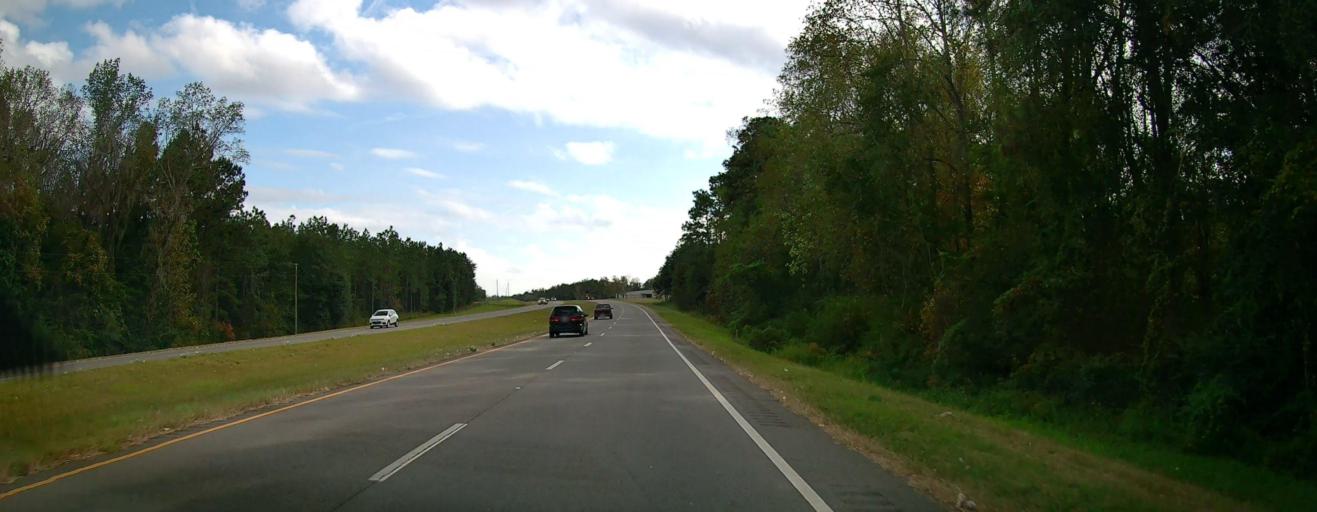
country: US
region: Georgia
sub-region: Thomas County
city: Meigs
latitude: 31.0498
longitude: -84.0709
